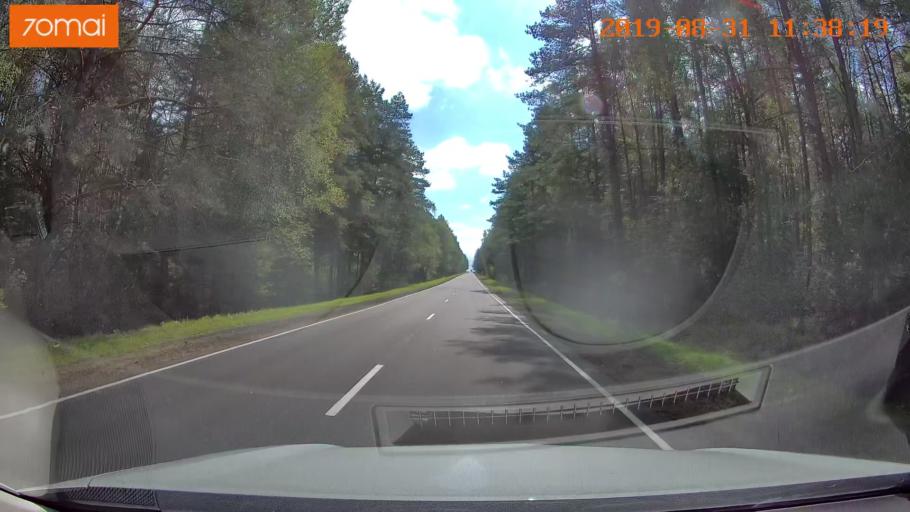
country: BY
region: Mogilev
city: Cherykaw
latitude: 53.6418
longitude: 31.2725
